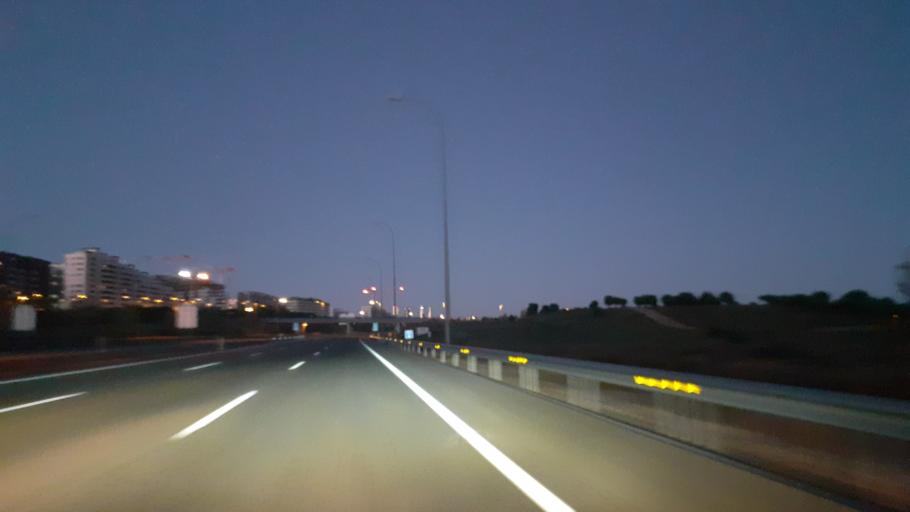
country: ES
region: Madrid
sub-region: Provincia de Madrid
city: Hortaleza
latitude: 40.5012
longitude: -3.6129
